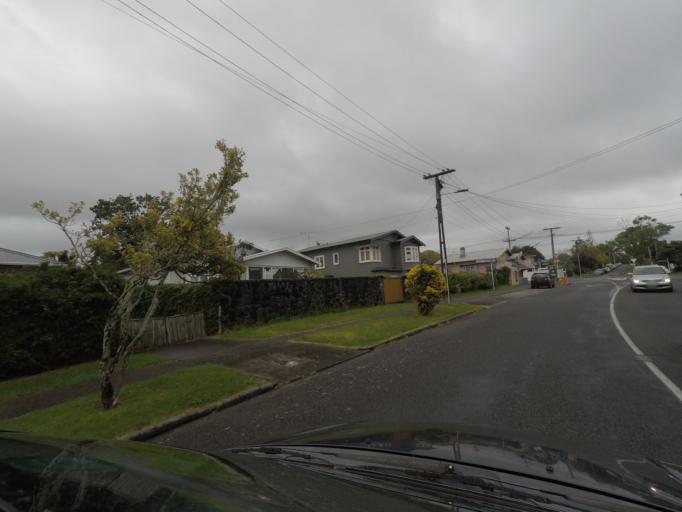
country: NZ
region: Auckland
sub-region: Auckland
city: Auckland
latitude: -36.8904
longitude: 174.7318
